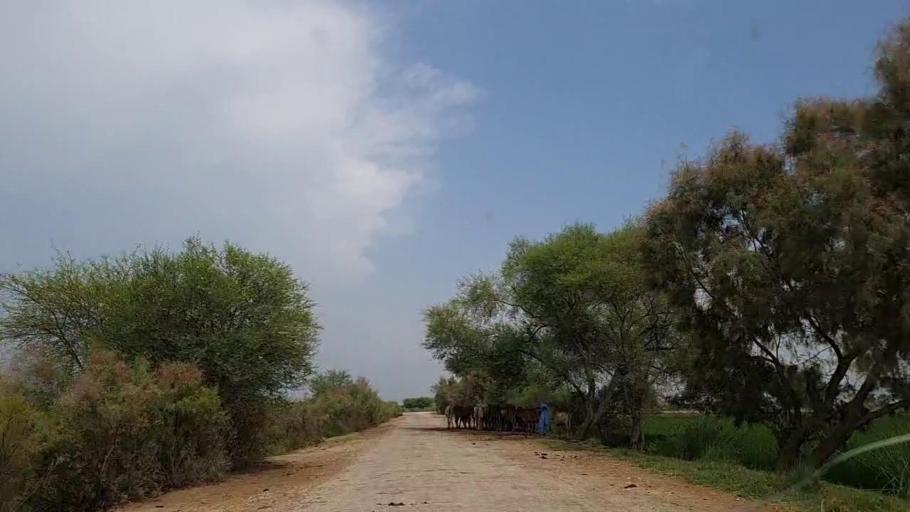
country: PK
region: Sindh
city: Khanpur
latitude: 27.8378
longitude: 69.4903
